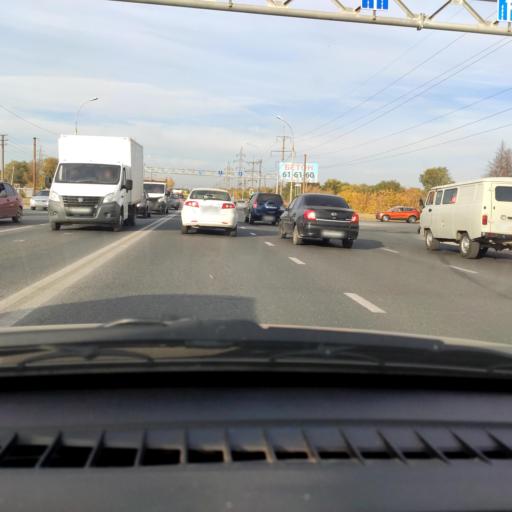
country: RU
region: Samara
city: Tol'yatti
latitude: 53.5634
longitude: 49.2901
